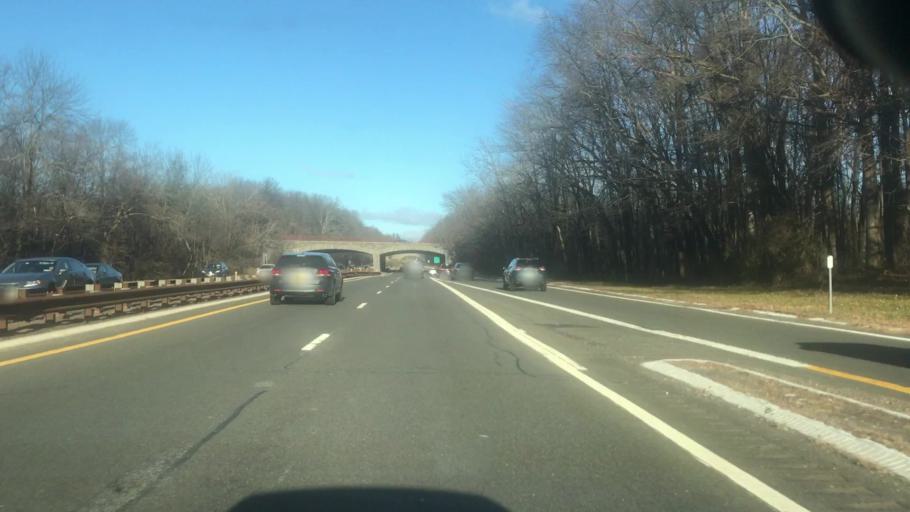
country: US
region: New York
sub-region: Rockland County
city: Bardonia
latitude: 41.1050
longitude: -73.9951
